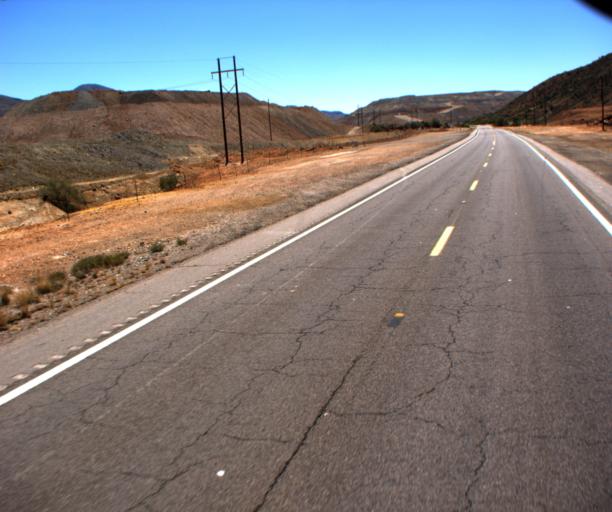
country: US
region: Arizona
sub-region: Pinal County
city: Kearny
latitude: 33.1687
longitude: -111.0086
